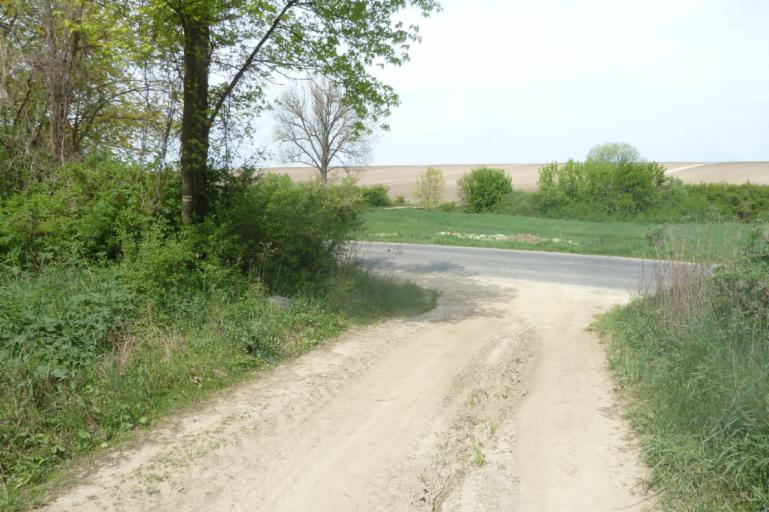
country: HU
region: Pest
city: Gomba
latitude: 47.3626
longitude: 19.5695
